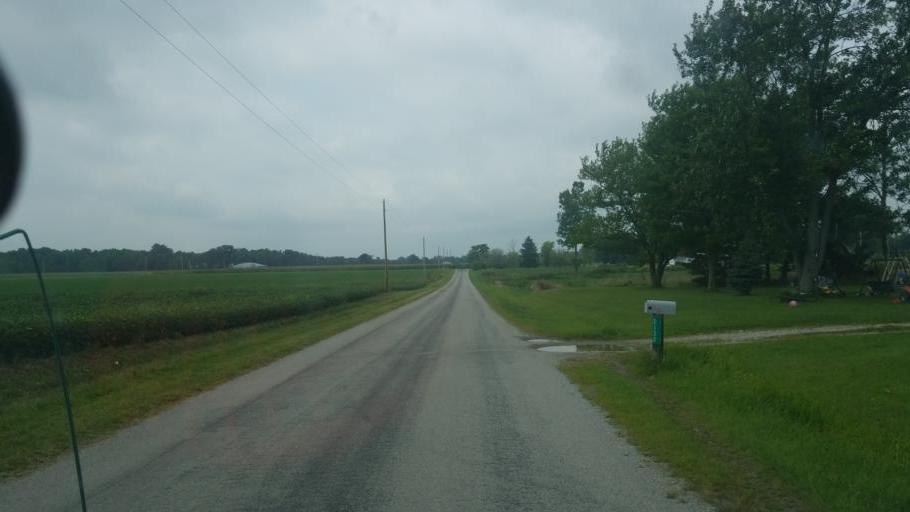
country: US
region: Ohio
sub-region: Huron County
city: Greenwich
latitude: 41.0108
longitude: -82.5053
